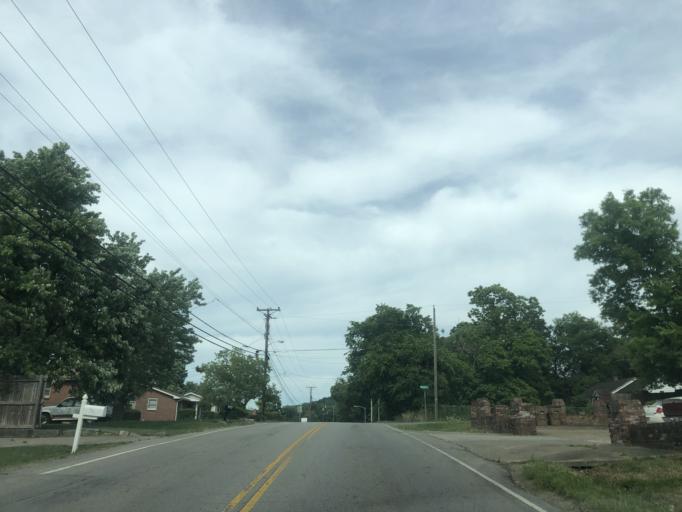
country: US
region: Tennessee
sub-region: Davidson County
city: Nashville
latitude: 36.2169
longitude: -86.8106
